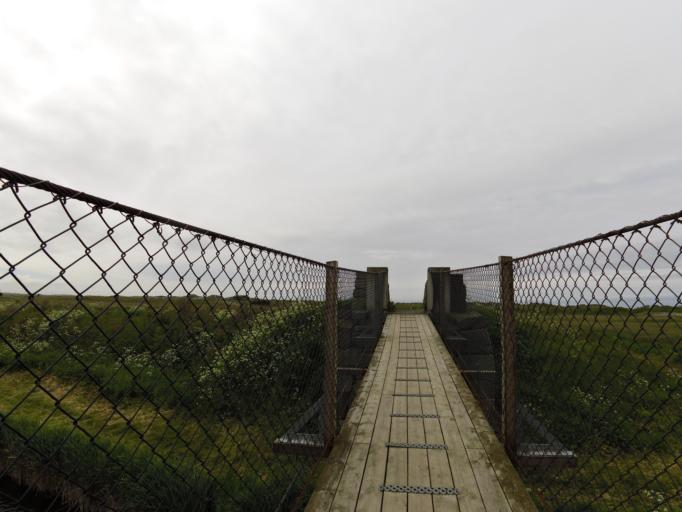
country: NO
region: Rogaland
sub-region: Klepp
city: Kleppe
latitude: 58.8108
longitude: 5.5522
